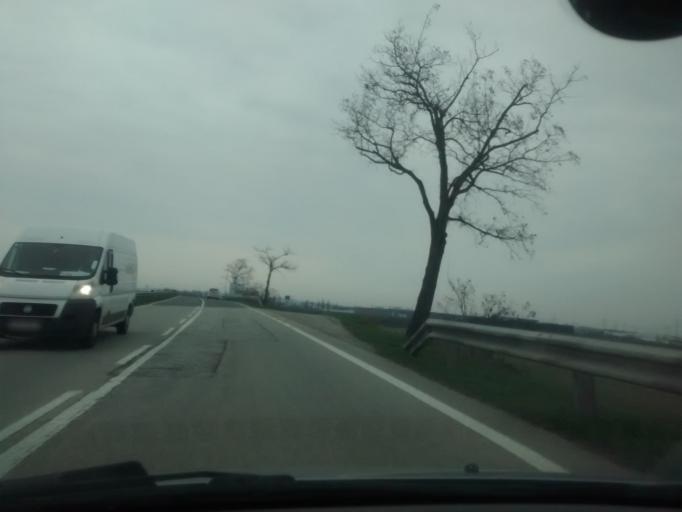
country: AT
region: Lower Austria
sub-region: Politischer Bezirk Modling
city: Achau
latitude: 48.0930
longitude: 16.3935
